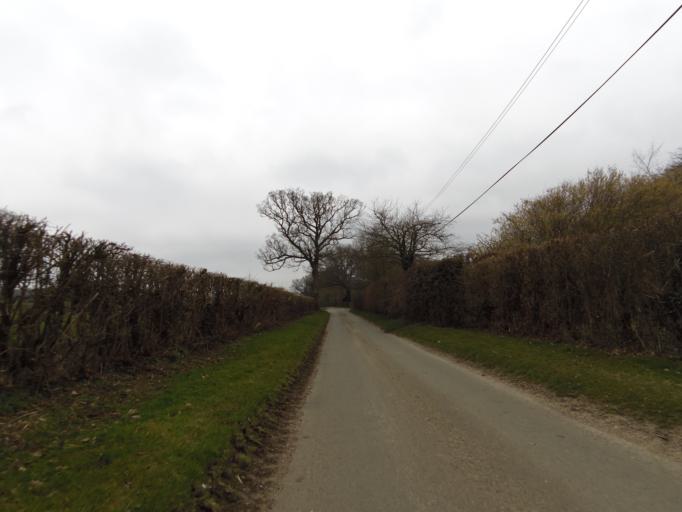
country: GB
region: England
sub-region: Suffolk
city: Framlingham
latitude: 52.2460
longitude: 1.3950
